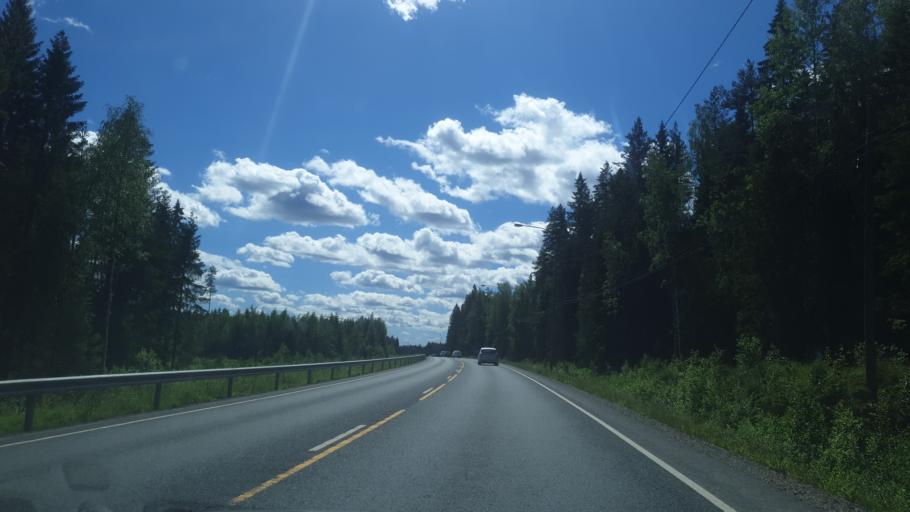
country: FI
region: Northern Savo
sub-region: Varkaus
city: Leppaevirta
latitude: 62.5559
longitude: 27.6195
